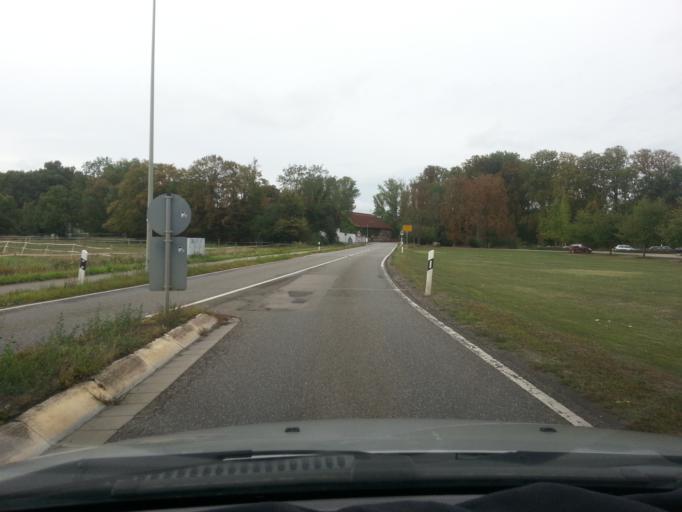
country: DE
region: Rheinland-Pfalz
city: Offenbach an der Queich
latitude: 49.2150
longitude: 8.1857
